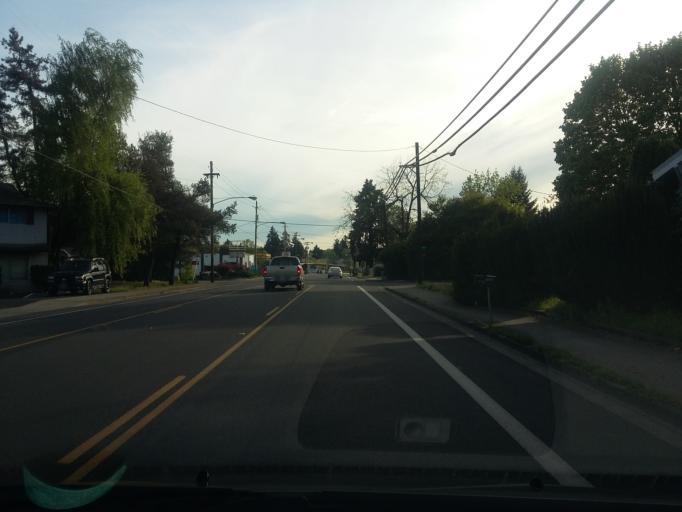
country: US
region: Washington
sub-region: Clark County
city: Minnehaha
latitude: 45.6436
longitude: -122.6455
